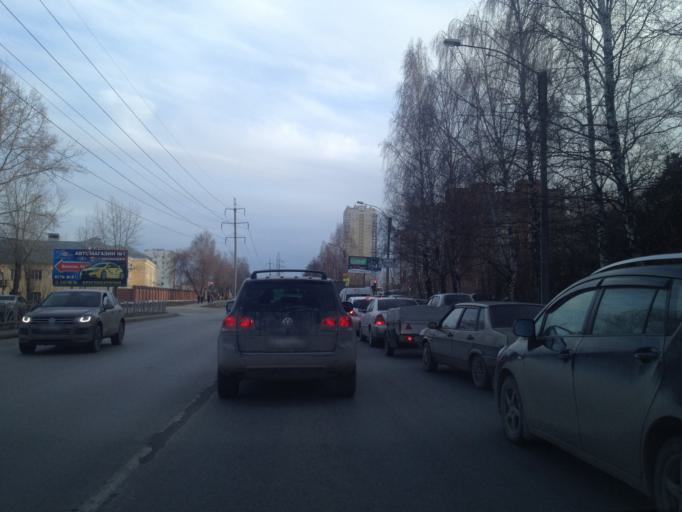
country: RU
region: Sverdlovsk
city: Sovkhoznyy
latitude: 56.7817
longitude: 60.5983
